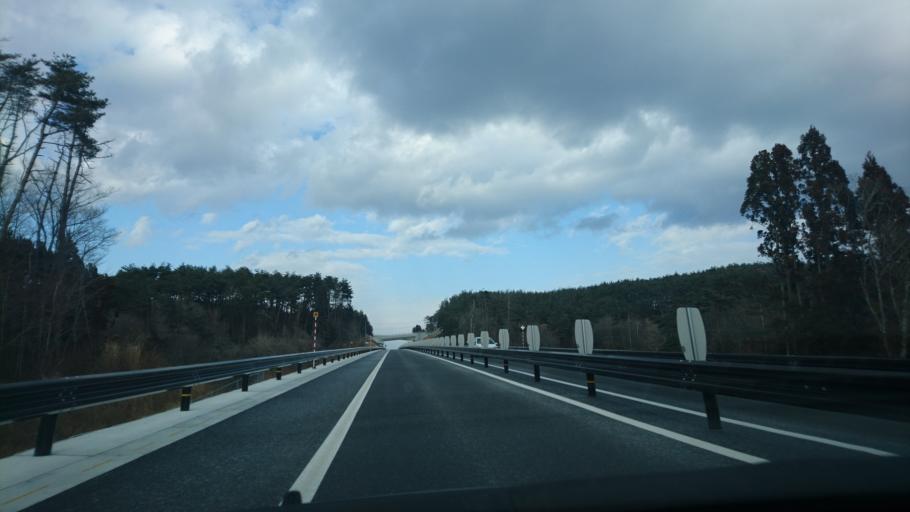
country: JP
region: Miyagi
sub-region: Oshika Gun
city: Onagawa Cho
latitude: 38.7271
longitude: 141.5152
